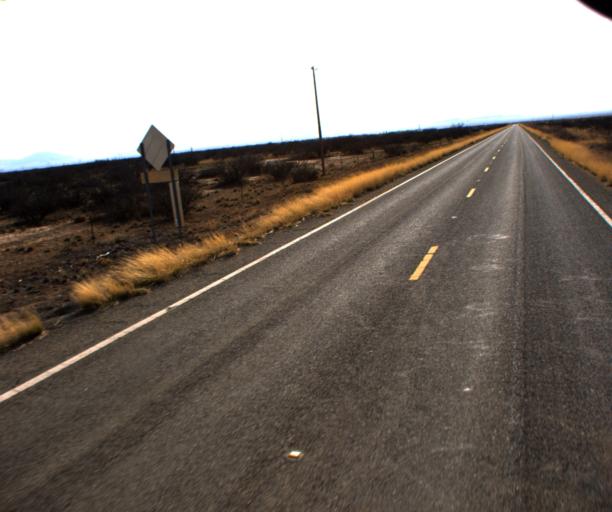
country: US
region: Arizona
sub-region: Cochise County
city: Willcox
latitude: 32.1953
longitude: -109.7428
